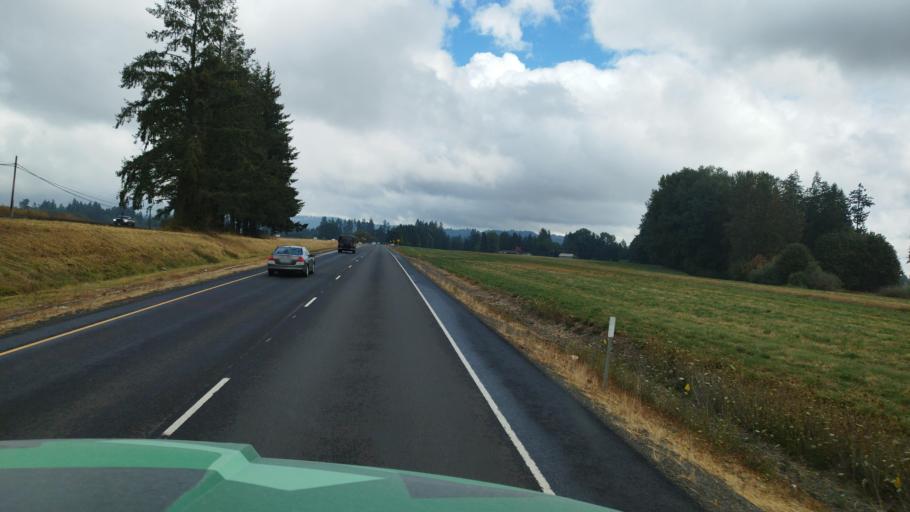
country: US
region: Oregon
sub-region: Yamhill County
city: Lafayette
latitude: 45.2425
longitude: -123.1321
